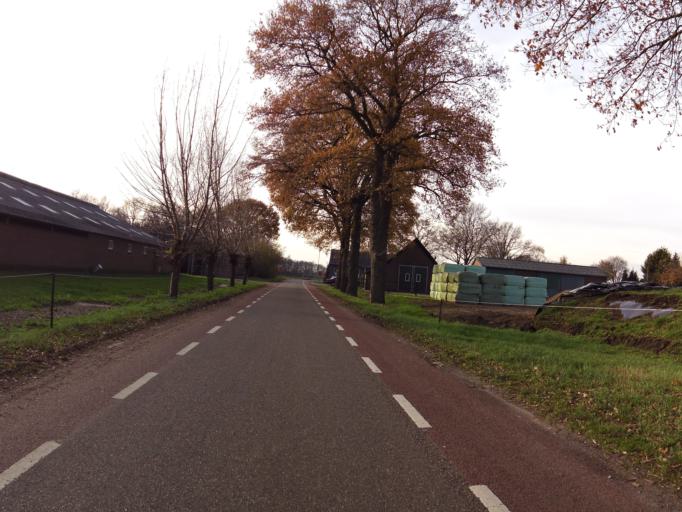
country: NL
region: North Brabant
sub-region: Gemeente Landerd
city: Zeeland
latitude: 51.6679
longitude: 5.6746
